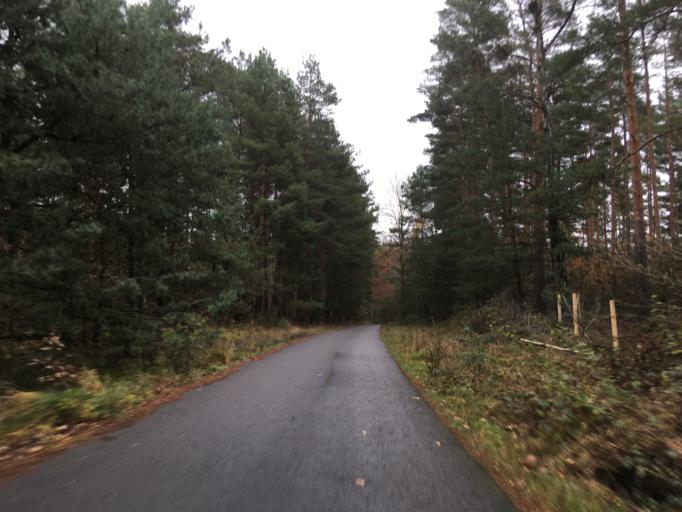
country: DE
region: Brandenburg
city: Jamlitz
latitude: 52.0414
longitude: 14.4754
